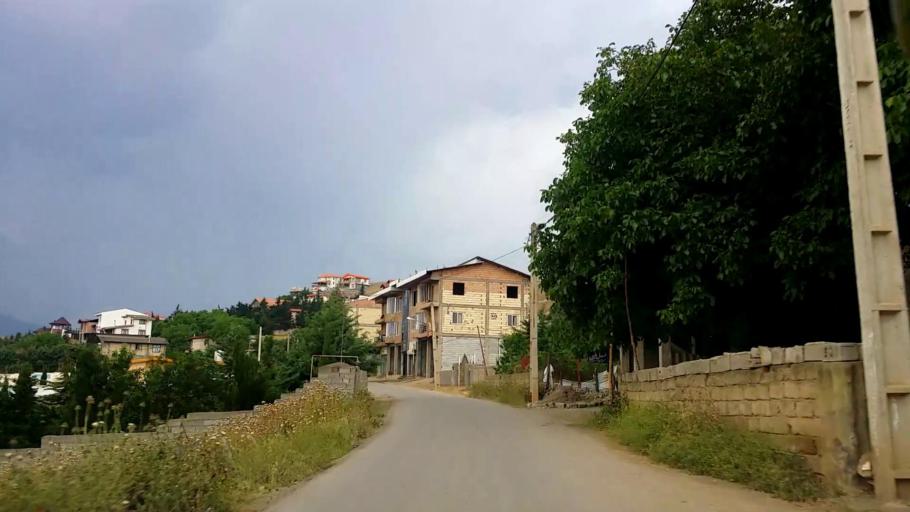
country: IR
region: Mazandaran
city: Chalus
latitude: 36.5148
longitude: 51.2534
